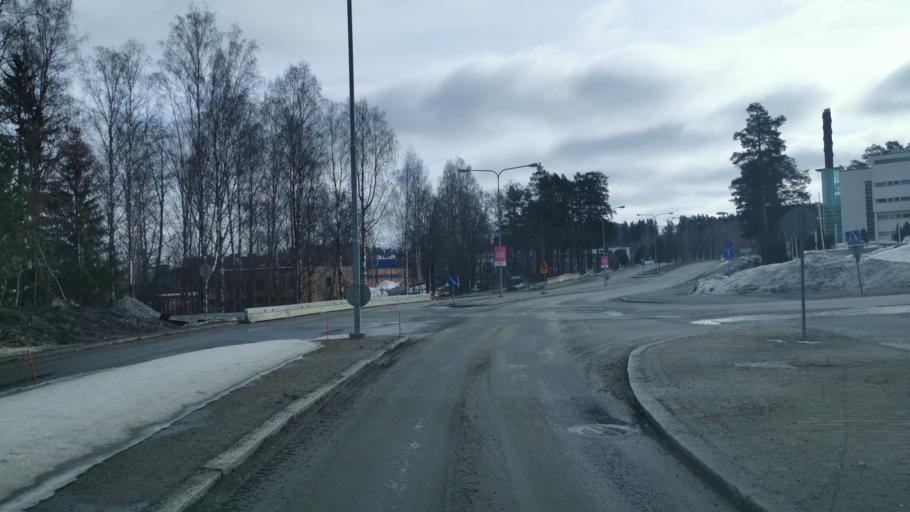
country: FI
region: Northern Savo
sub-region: Kuopio
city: Kuopio
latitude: 62.8911
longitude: 27.6293
